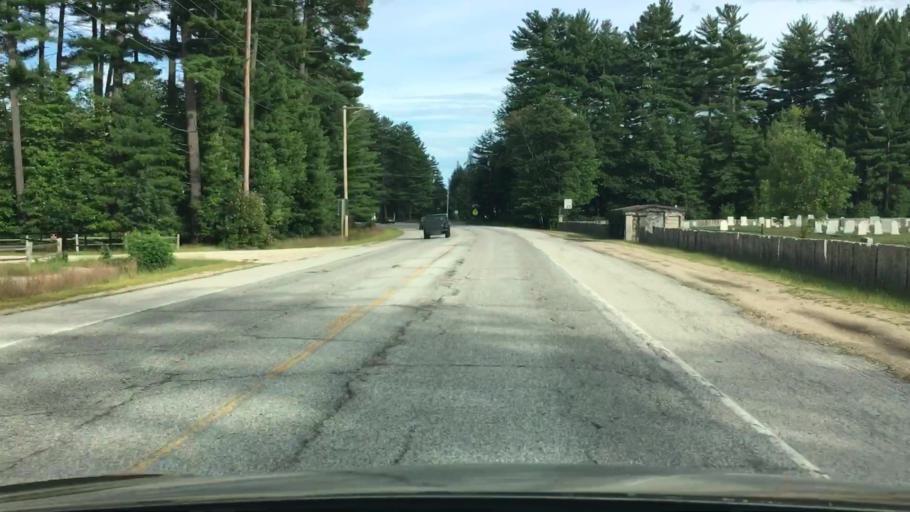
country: US
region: Maine
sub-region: Oxford County
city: Fryeburg
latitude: 44.0206
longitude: -70.9715
